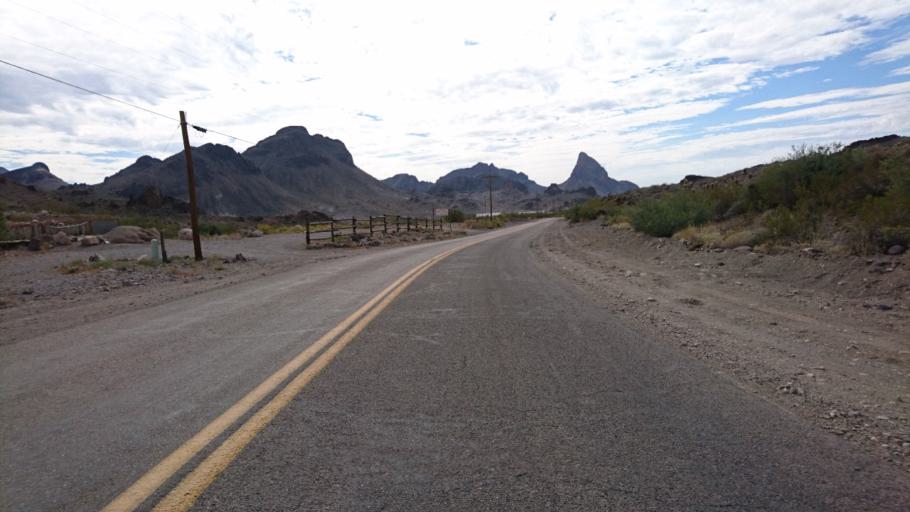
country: US
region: Arizona
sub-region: Mohave County
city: Mohave Valley
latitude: 35.0139
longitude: -114.3876
